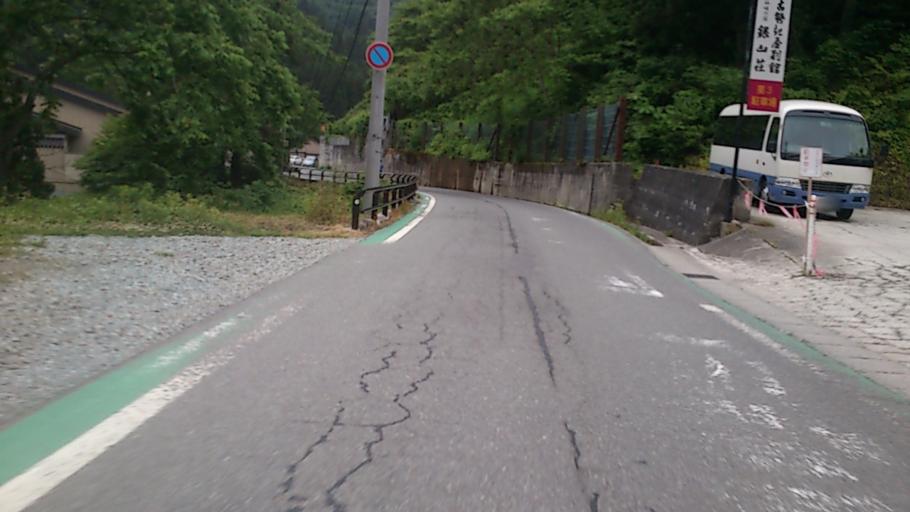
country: JP
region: Yamagata
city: Obanazawa
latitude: 38.5726
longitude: 140.5269
